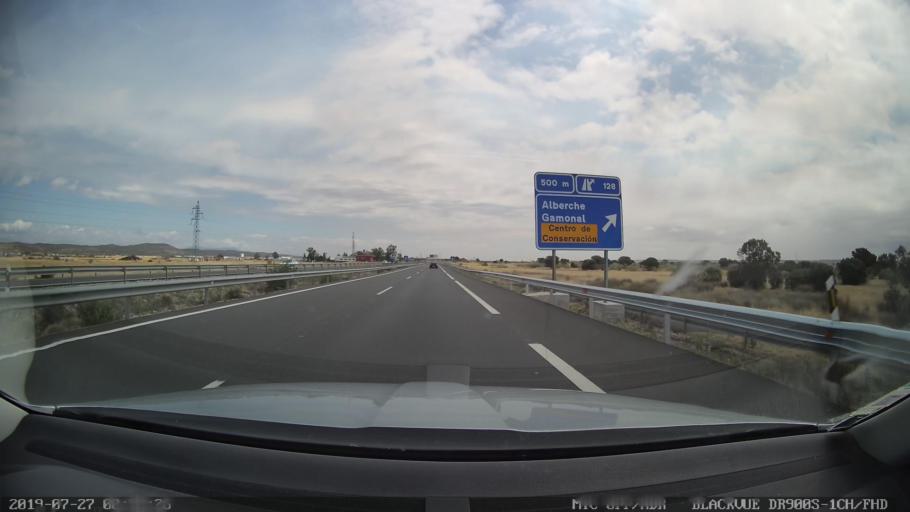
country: ES
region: Castille-La Mancha
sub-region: Province of Toledo
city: Velada
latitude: 39.9394
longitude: -4.9617
